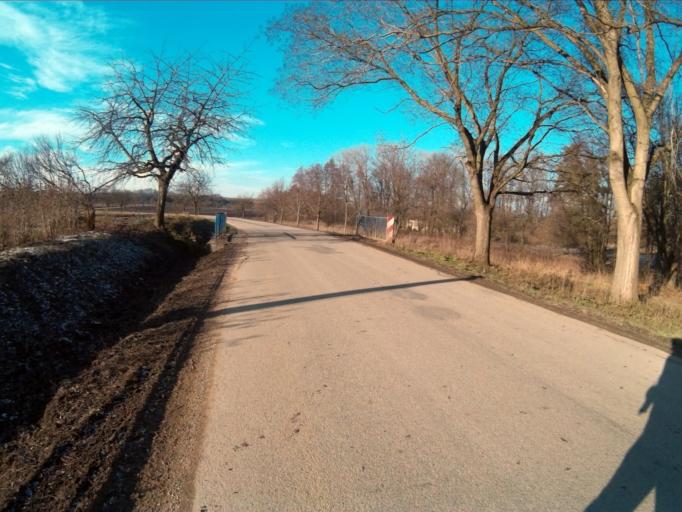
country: CZ
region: South Moravian
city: Krenovice
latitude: 49.1509
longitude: 16.8255
